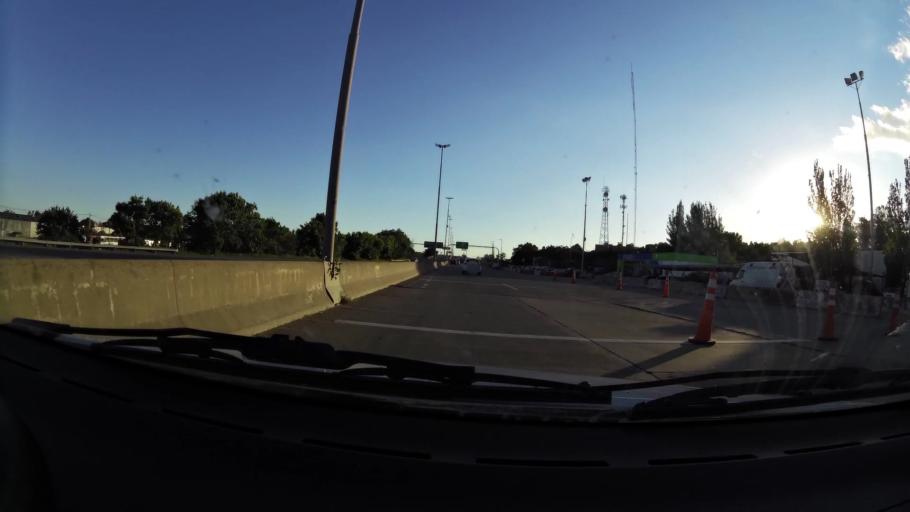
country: AR
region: Buenos Aires
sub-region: Partido de Quilmes
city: Quilmes
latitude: -34.7861
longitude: -58.1543
